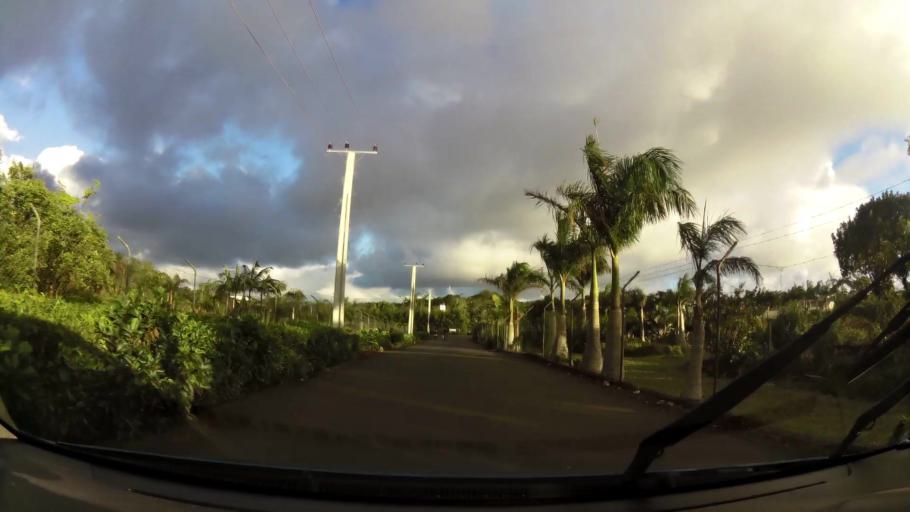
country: MU
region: Plaines Wilhems
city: Curepipe
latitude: -20.3058
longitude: 57.5346
